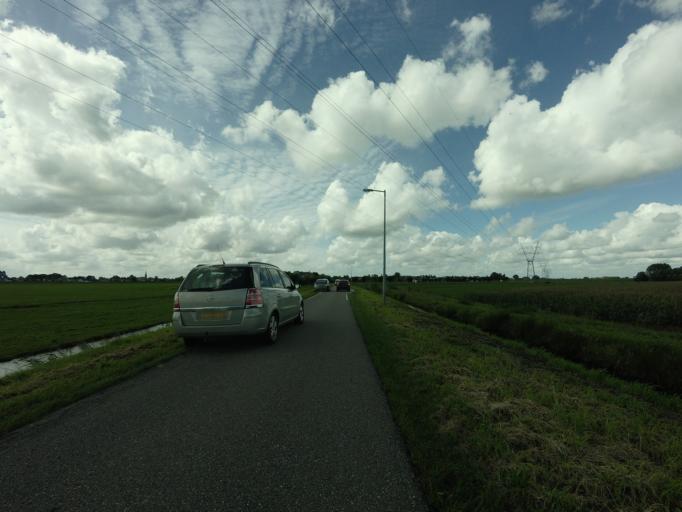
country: NL
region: North Holland
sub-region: Gemeente Purmerend
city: Purmerend
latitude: 52.4642
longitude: 4.9632
